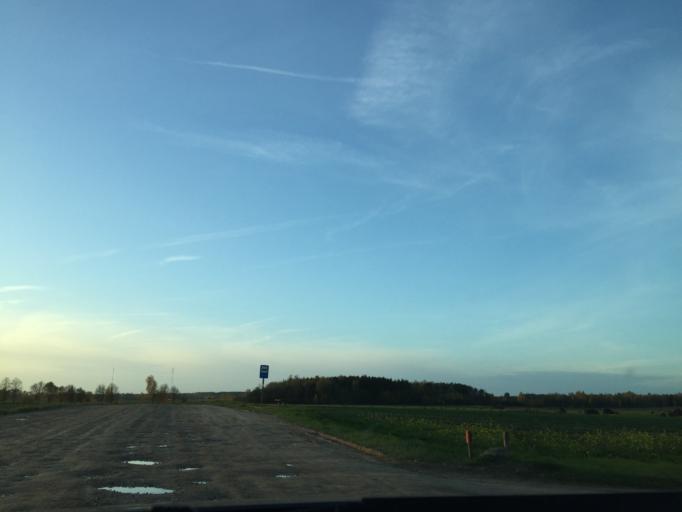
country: LV
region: Malpils
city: Malpils
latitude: 56.8847
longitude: 24.9613
